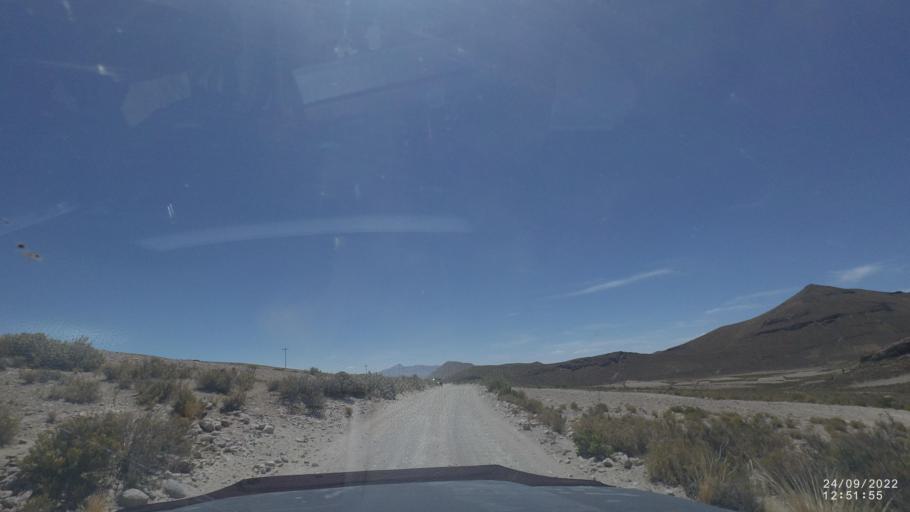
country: BO
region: Potosi
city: Colchani
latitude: -19.8133
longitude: -67.5669
